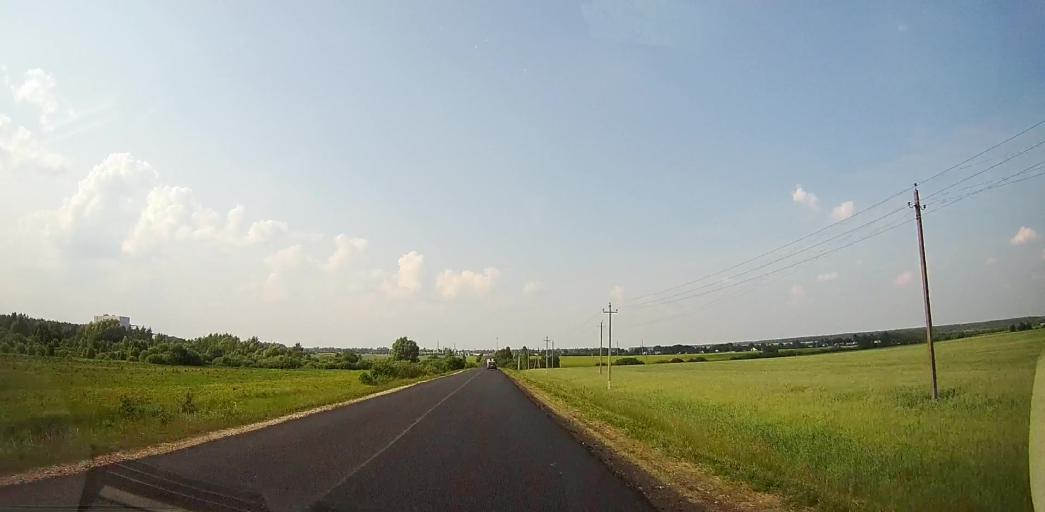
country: RU
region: Moskovskaya
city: Barybino
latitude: 55.2388
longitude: 37.9191
